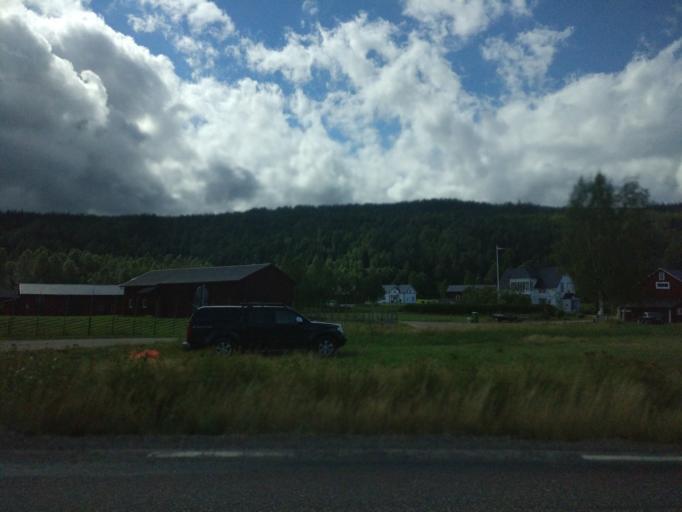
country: SE
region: Vaermland
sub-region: Hagfors Kommun
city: Ekshaerad
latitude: 60.2866
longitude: 13.3986
